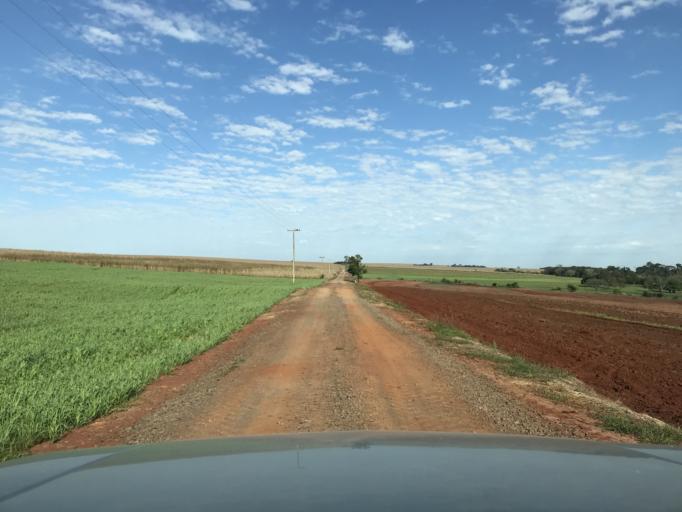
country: BR
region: Parana
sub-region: Palotina
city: Palotina
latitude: -24.1628
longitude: -53.7484
